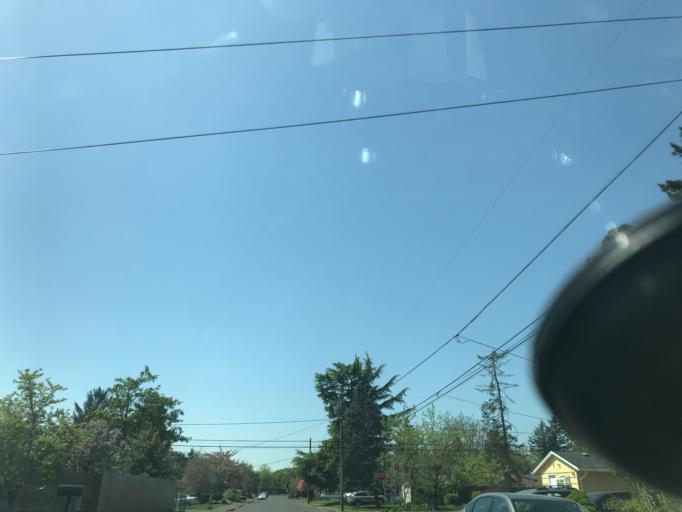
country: US
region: Oregon
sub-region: Multnomah County
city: Lents
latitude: 45.4908
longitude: -122.5616
